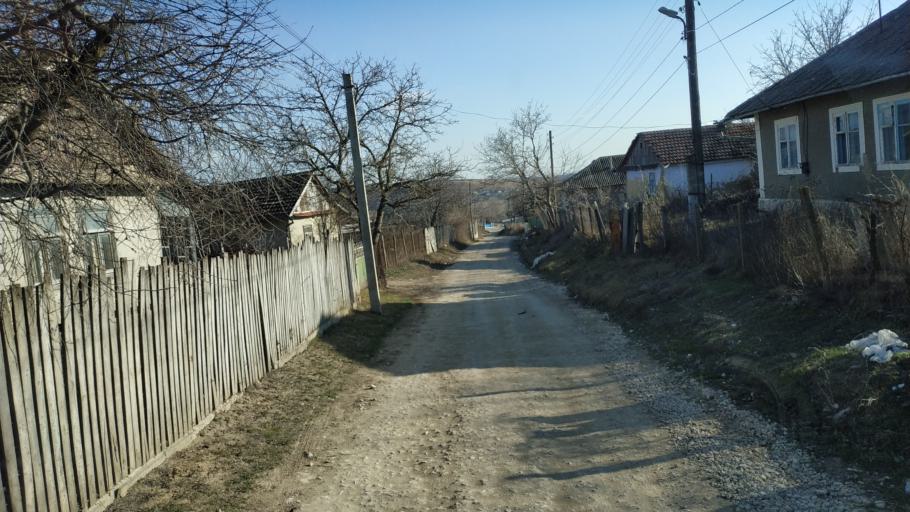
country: MD
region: Hincesti
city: Hincesti
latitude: 46.7325
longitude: 28.5124
